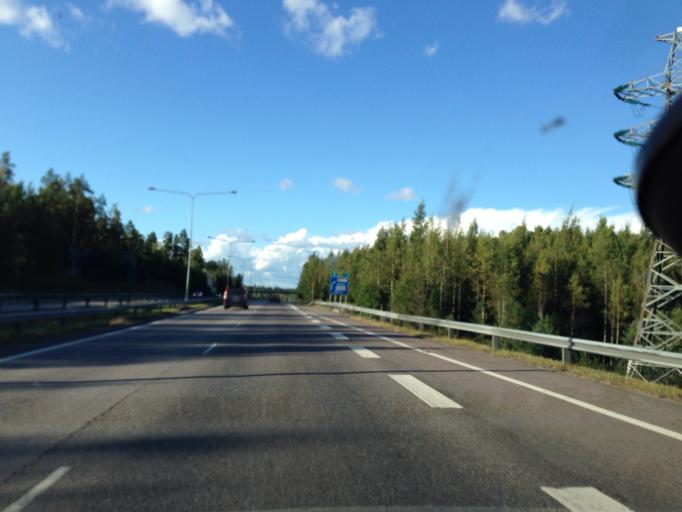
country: FI
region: Uusimaa
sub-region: Helsinki
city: Vantaa
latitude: 60.3284
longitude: 24.9987
